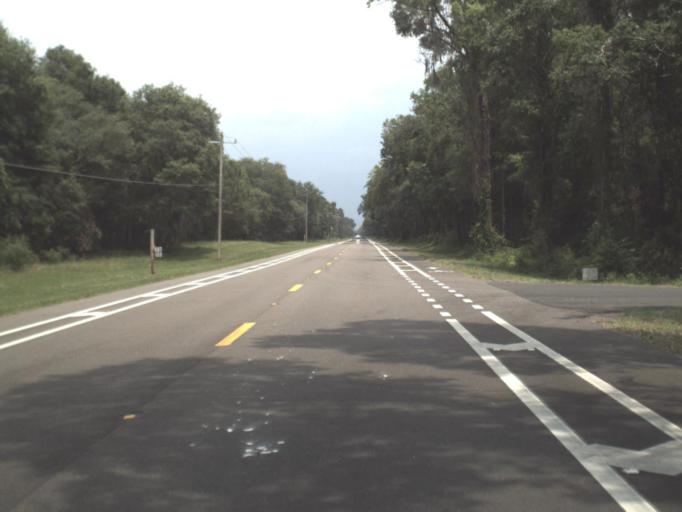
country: US
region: Florida
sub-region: Levy County
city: Manatee Road
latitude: 29.4964
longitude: -82.9268
